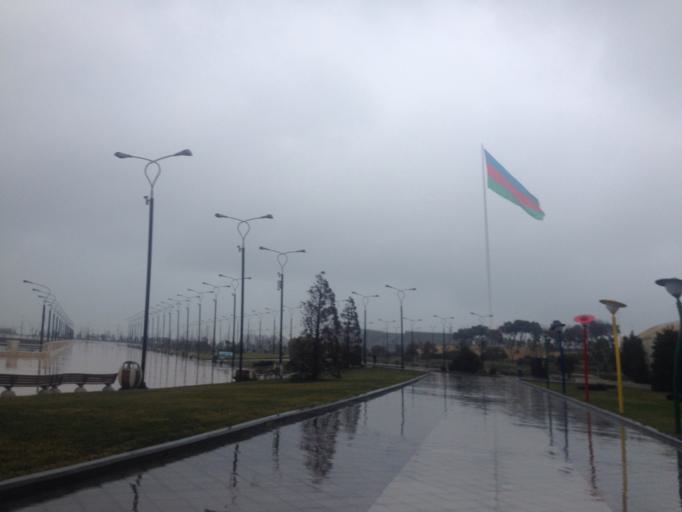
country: AZ
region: Baki
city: Badamdar
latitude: 40.3472
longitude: 49.8399
